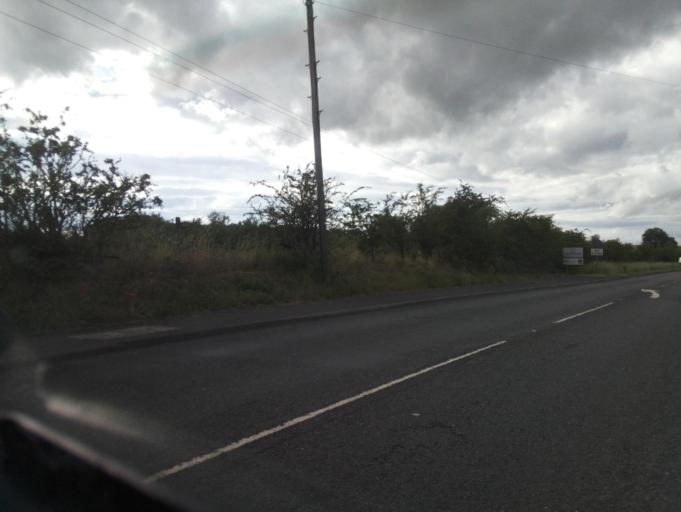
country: GB
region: England
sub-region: Worcestershire
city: Kidderminster
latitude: 52.4324
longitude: -2.2120
